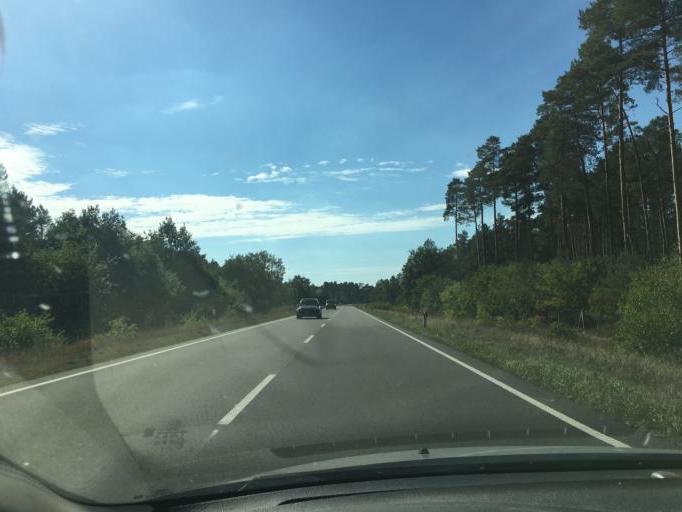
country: DE
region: Brandenburg
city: Weisen
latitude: 53.0406
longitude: 11.8110
